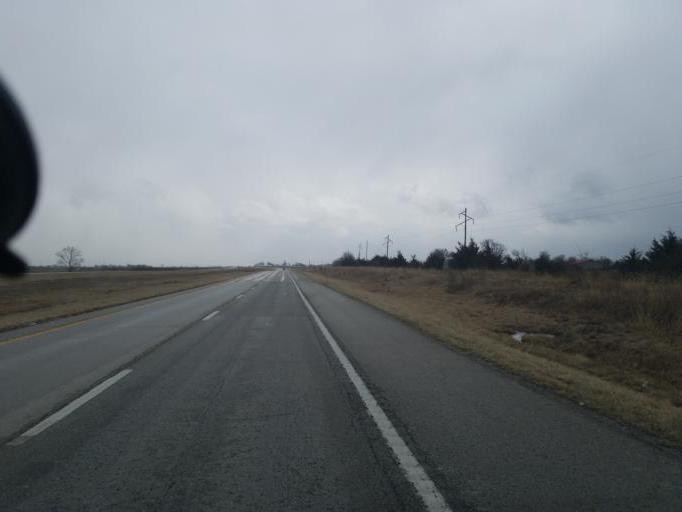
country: US
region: Missouri
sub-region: Randolph County
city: Moberly
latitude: 39.5371
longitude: -92.4480
